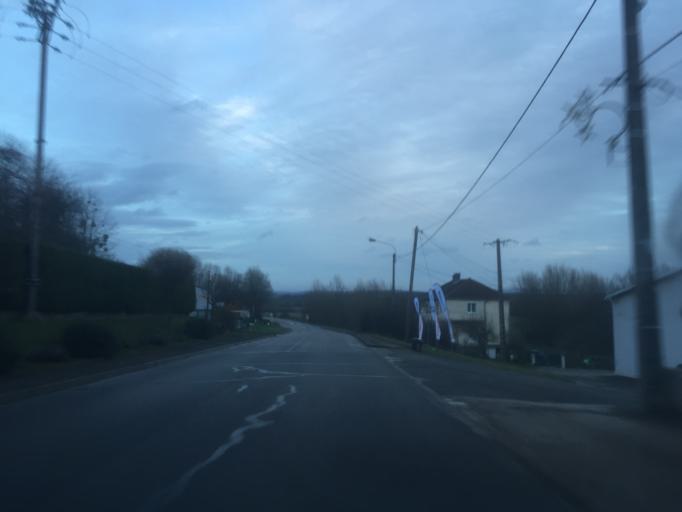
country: FR
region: Franche-Comte
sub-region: Departement du Jura
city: Orchamps
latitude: 47.1460
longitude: 5.6650
